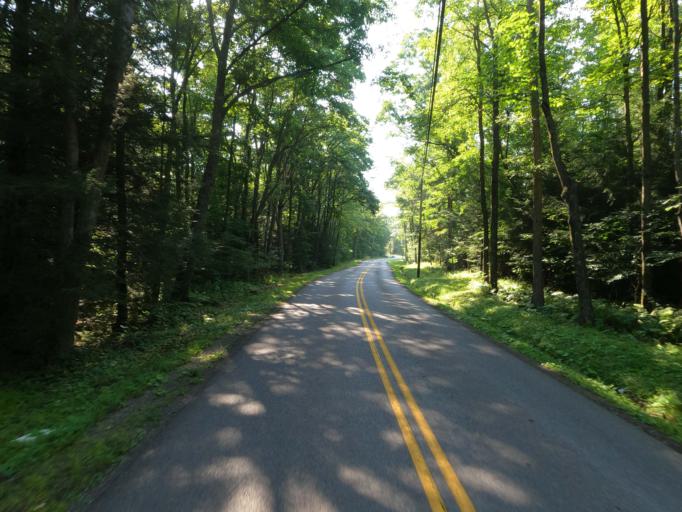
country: US
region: Maryland
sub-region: Garrett County
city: Oakland
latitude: 39.4962
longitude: -79.3893
